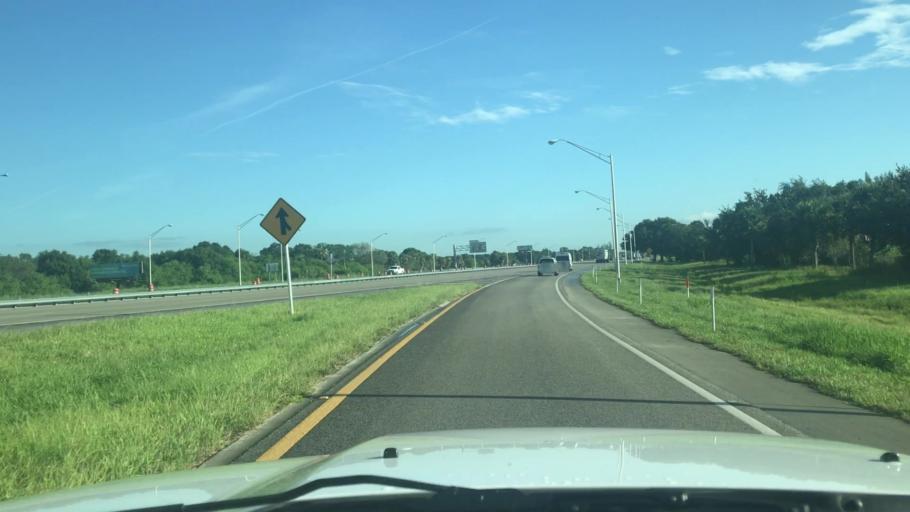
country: US
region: Florida
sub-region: Saint Lucie County
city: Fort Pierce South
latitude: 27.4196
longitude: -80.3879
